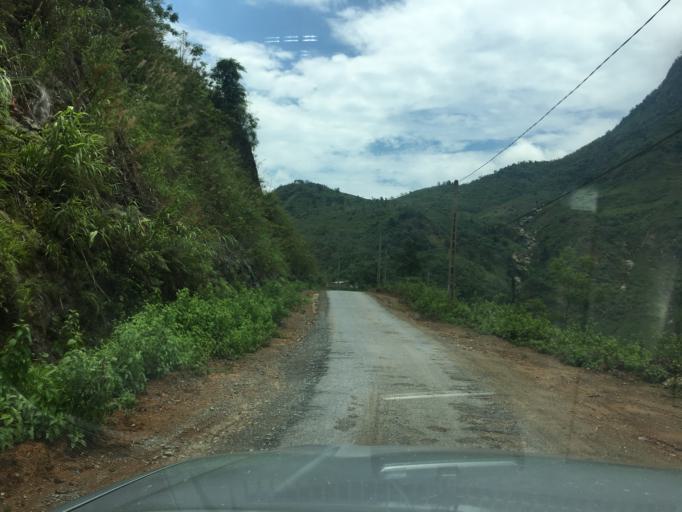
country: VN
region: Yen Bai
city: Son Thinh
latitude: 21.6786
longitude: 104.5544
